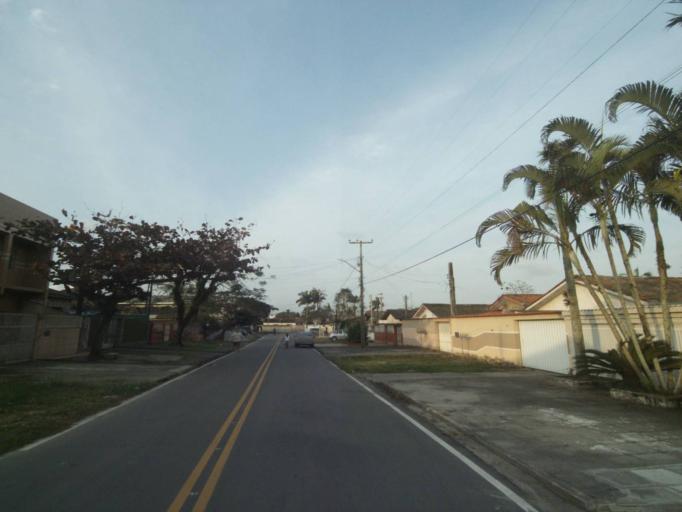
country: BR
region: Parana
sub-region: Paranagua
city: Paranagua
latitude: -25.5140
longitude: -48.5411
